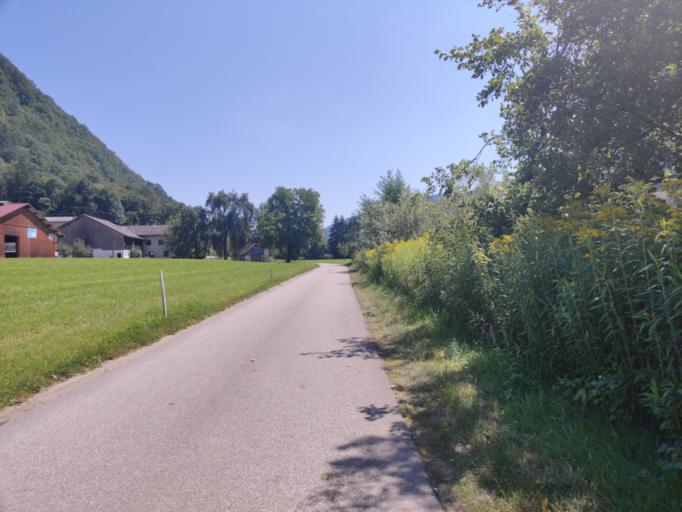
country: AT
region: Upper Austria
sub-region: Politischer Bezirk Rohrbach
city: Pfarrkirchen im Muehlkreis
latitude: 48.4541
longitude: 13.8228
